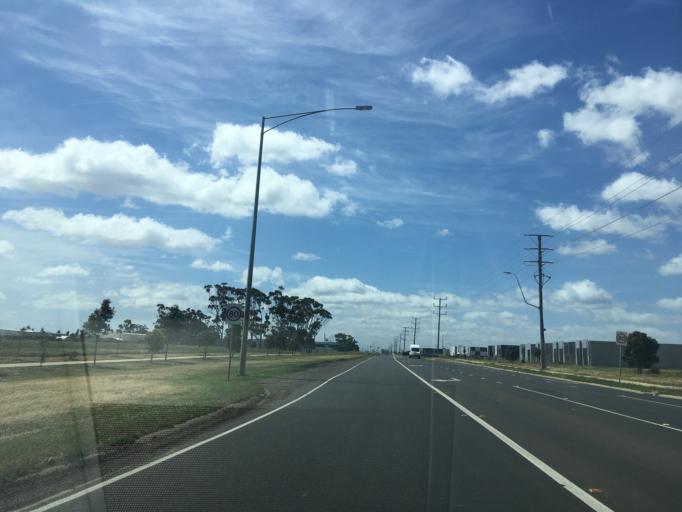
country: AU
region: Victoria
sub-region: Wyndham
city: Truganina
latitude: -37.8240
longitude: 144.7378
